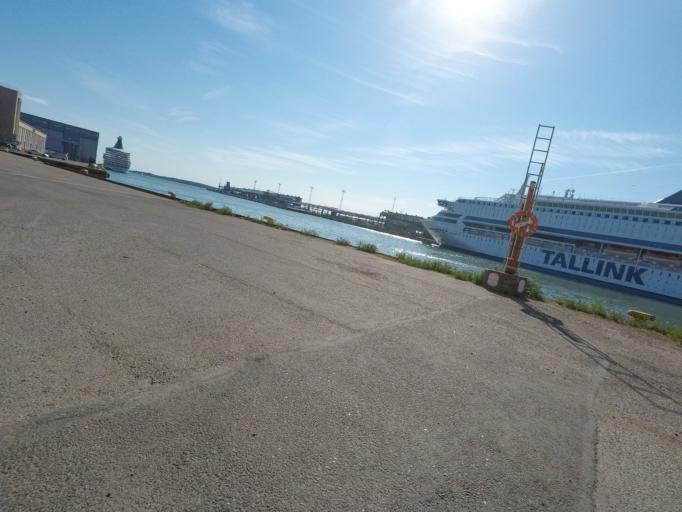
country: FI
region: Uusimaa
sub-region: Helsinki
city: Helsinki
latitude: 60.1544
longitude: 24.9262
